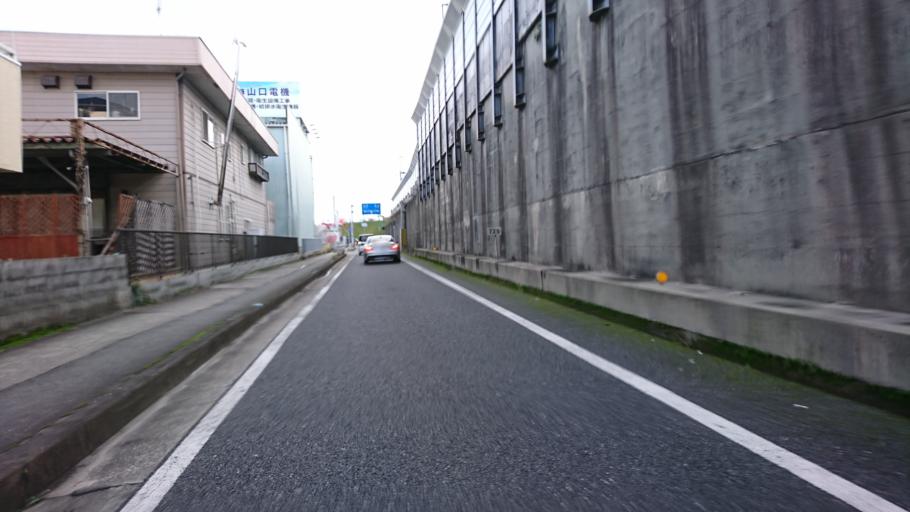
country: JP
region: Hyogo
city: Kakogawacho-honmachi
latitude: 34.7787
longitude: 134.8361
